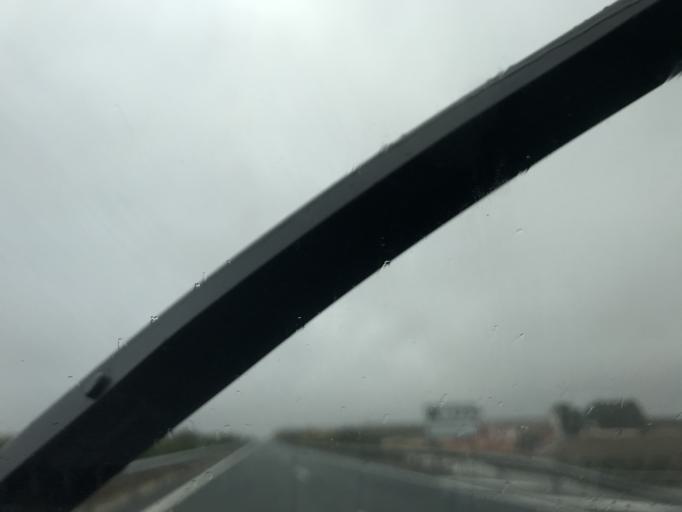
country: ES
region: Andalusia
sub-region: Provincia de Malaga
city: Mollina
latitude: 37.1171
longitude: -4.6657
